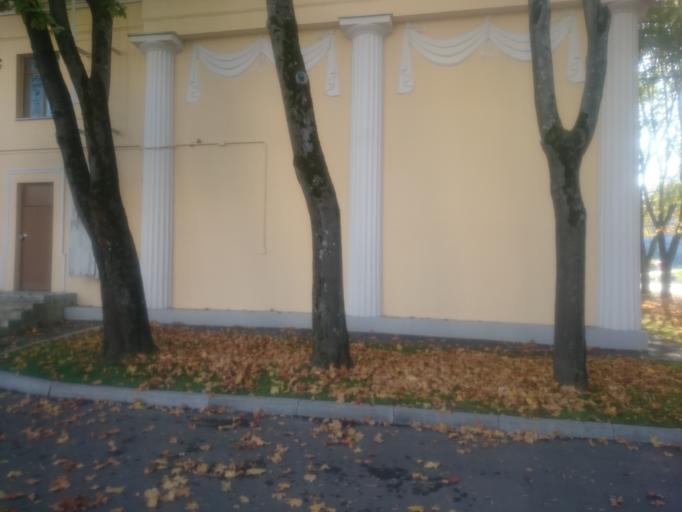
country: RU
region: Moscow
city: Ostankinskiy
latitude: 55.8352
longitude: 37.6197
